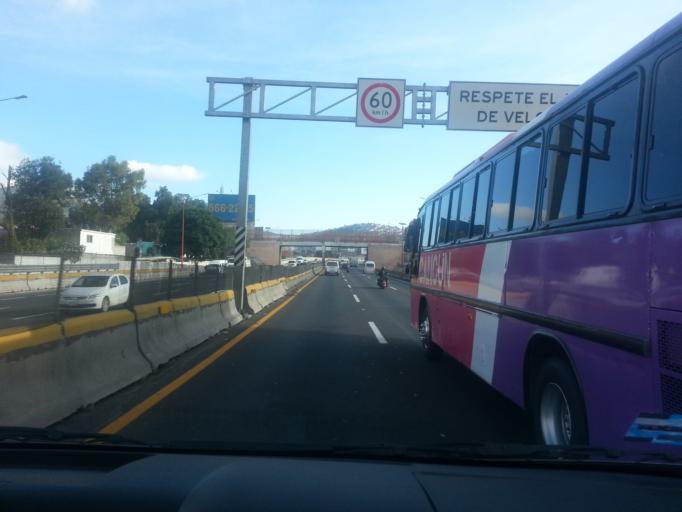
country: MX
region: Mexico
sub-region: Tlalnepantla de Baz
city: Puerto Escondido (Tepeolulco Puerto Escondido)
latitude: 19.5440
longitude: -99.0725
